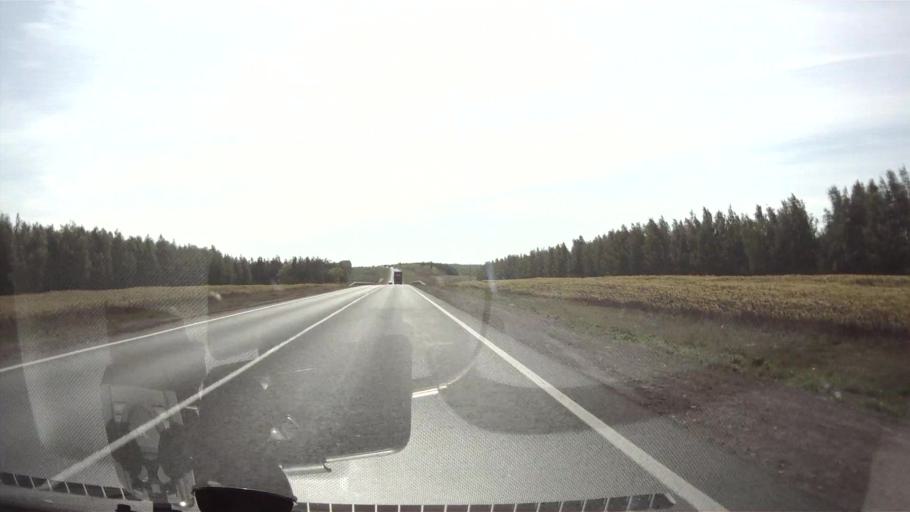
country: RU
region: Samara
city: Syzran'
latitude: 52.9048
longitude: 48.2977
